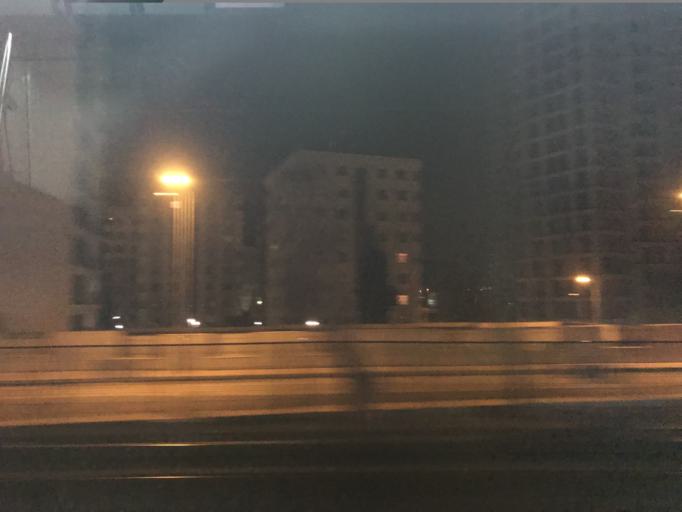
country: TR
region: Istanbul
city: Maltepe
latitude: 40.8943
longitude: 29.1747
